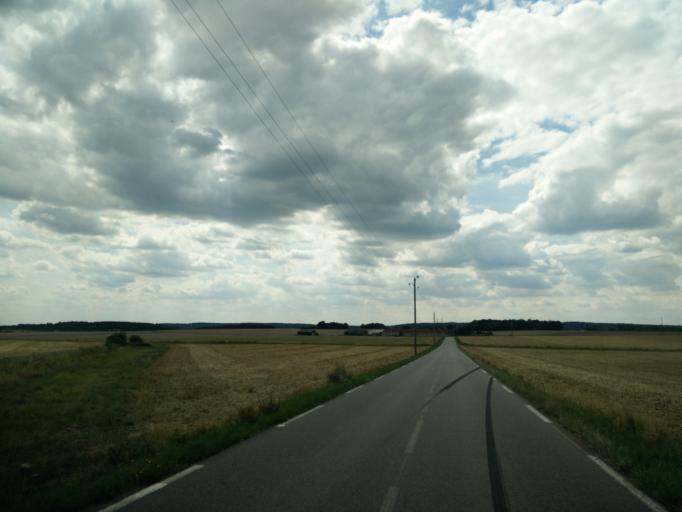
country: FR
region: Ile-de-France
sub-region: Departement des Yvelines
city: Garancieres
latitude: 48.8417
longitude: 1.7677
